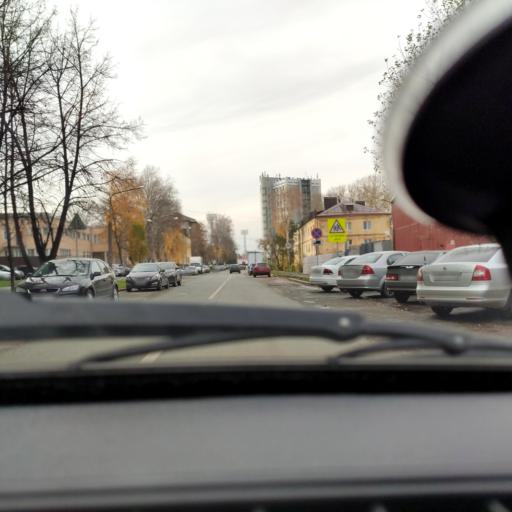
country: RU
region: Bashkortostan
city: Ufa
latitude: 54.8254
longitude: 56.0690
